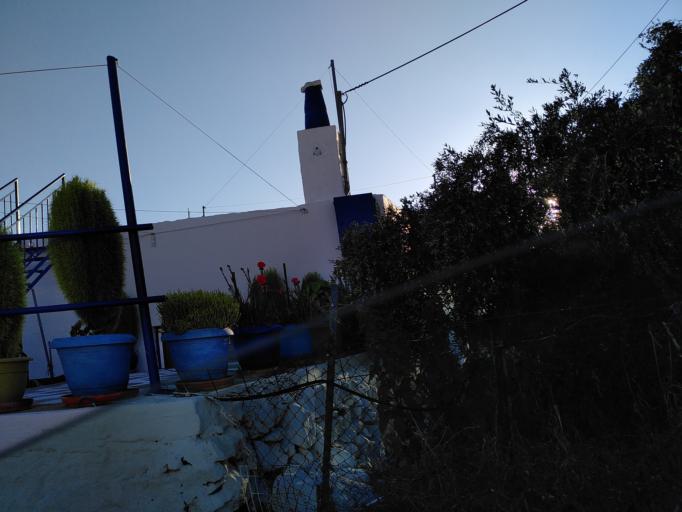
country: GR
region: South Aegean
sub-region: Nomos Kykladon
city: Amorgos
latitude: 36.9072
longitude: 25.9784
